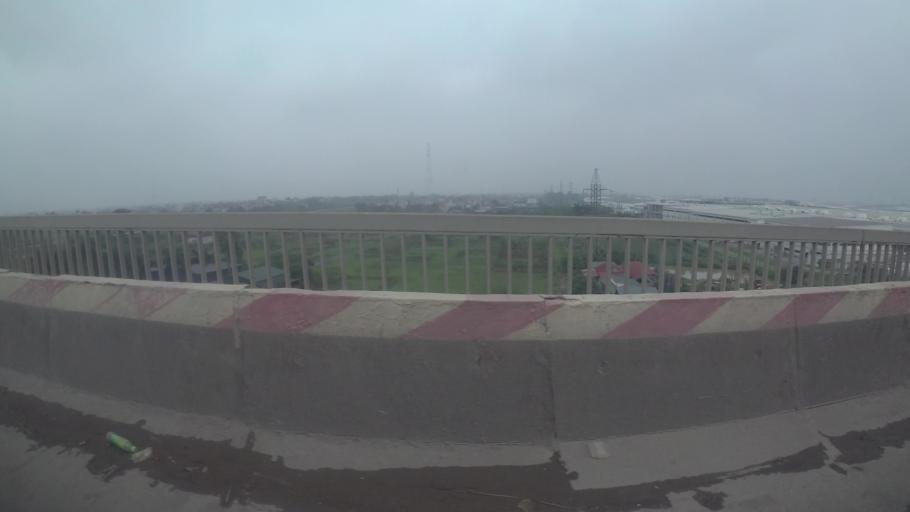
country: VN
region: Ha Noi
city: Tay Ho
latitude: 21.1083
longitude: 105.7870
